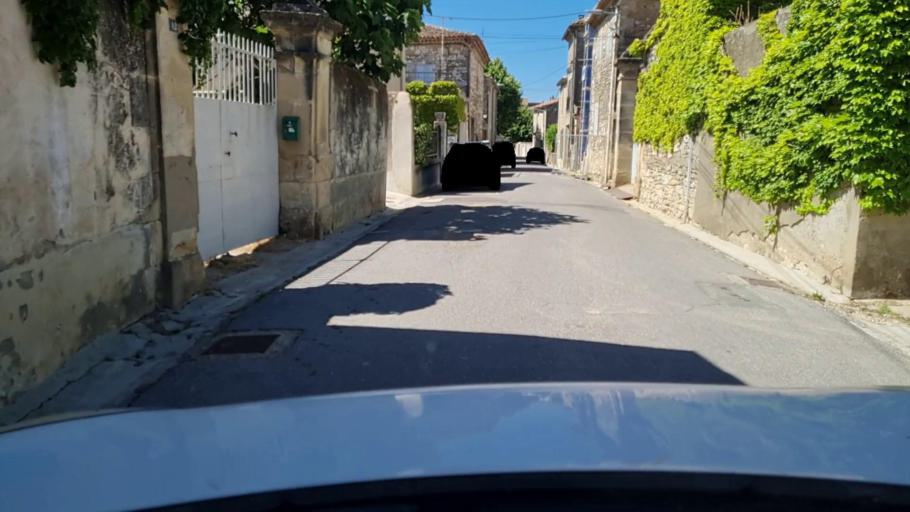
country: FR
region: Languedoc-Roussillon
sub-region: Departement du Gard
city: Saint-Mamert-du-Gard
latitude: 43.8524
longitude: 4.1575
